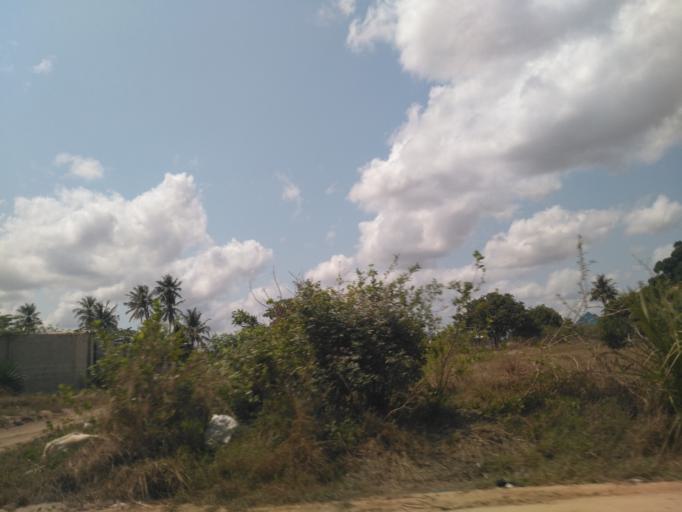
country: TZ
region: Dar es Salaam
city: Dar es Salaam
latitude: -6.8980
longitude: 39.3415
